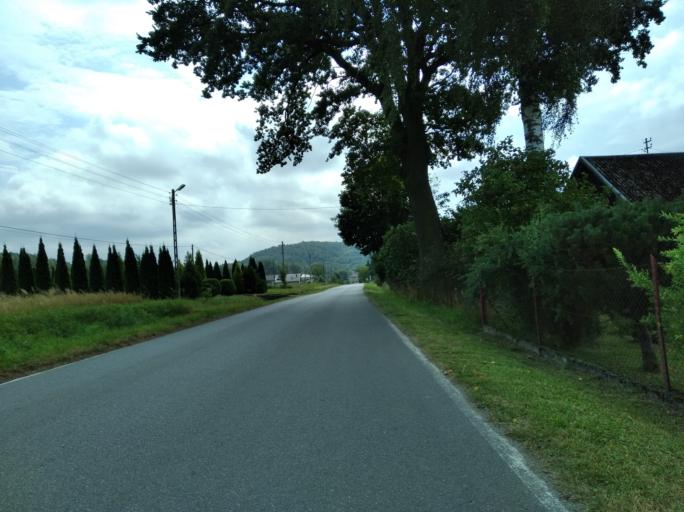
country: PL
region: Subcarpathian Voivodeship
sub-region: Powiat krosnienski
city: Wojaszowka
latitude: 49.7919
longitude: 21.6888
